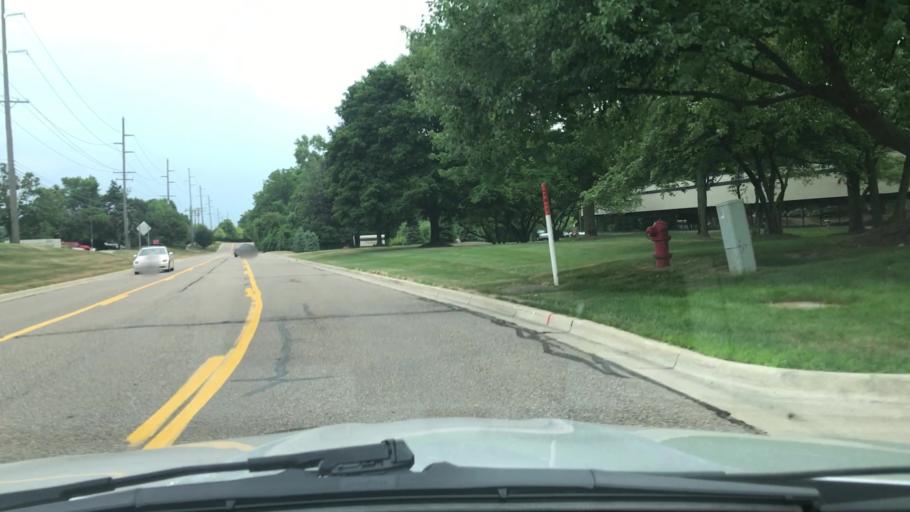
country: US
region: Michigan
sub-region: Wayne County
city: Northville
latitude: 42.4441
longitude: -83.4388
